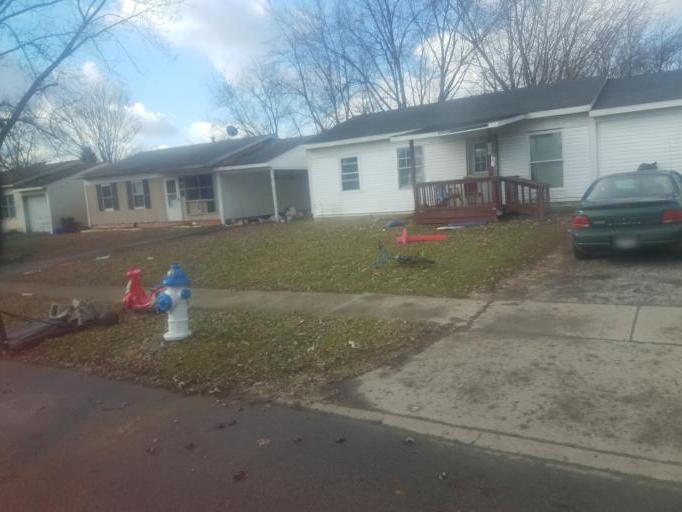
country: US
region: Ohio
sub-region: Marion County
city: Marion
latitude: 40.5806
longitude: -83.1518
